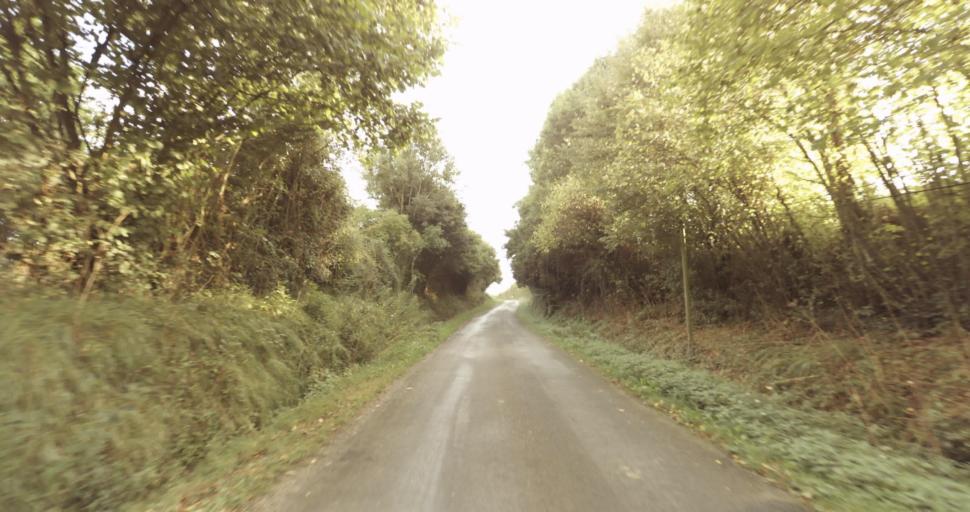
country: FR
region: Lower Normandy
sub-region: Departement de l'Orne
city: Sees
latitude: 48.6938
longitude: 0.2300
